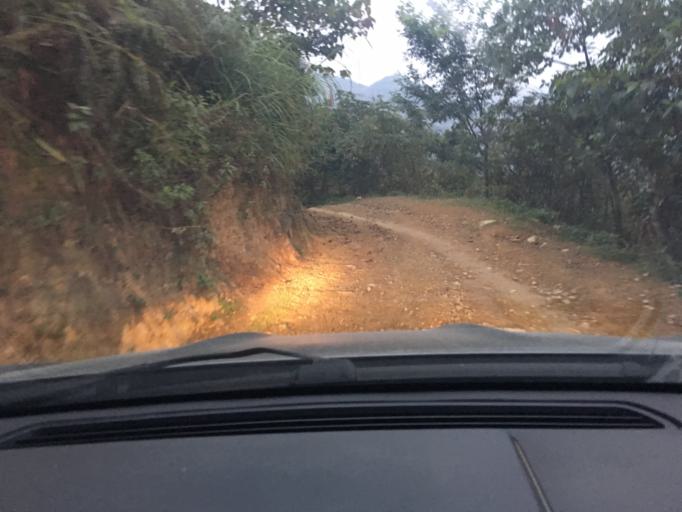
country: CN
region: Guangxi Zhuangzu Zizhiqu
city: Xinzhou
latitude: 24.9028
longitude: 105.5889
